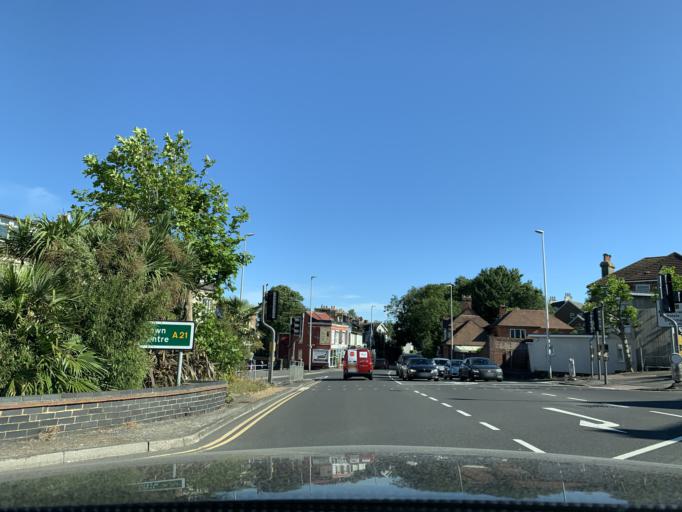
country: GB
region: England
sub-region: East Sussex
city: Saint Leonards-on-Sea
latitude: 50.8679
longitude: 0.5555
